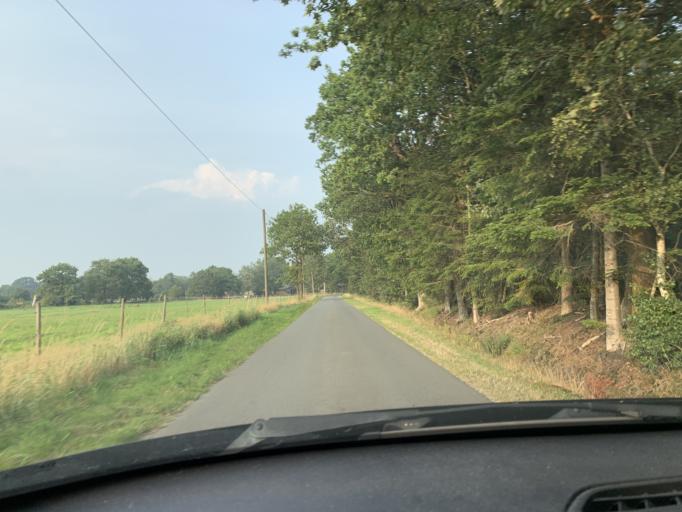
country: DE
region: Lower Saxony
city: Apen
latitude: 53.2557
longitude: 7.8425
